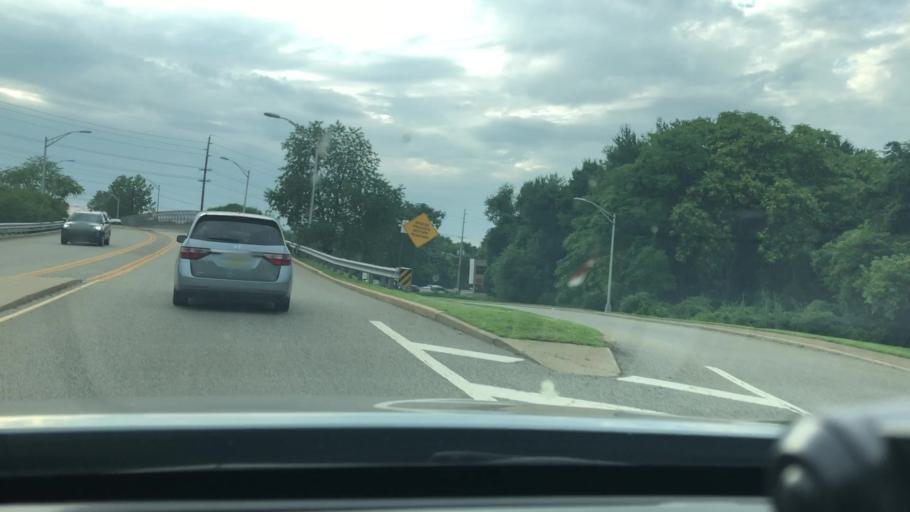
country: US
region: New Jersey
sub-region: Bergen County
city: Paramus
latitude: 40.9592
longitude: -74.0733
